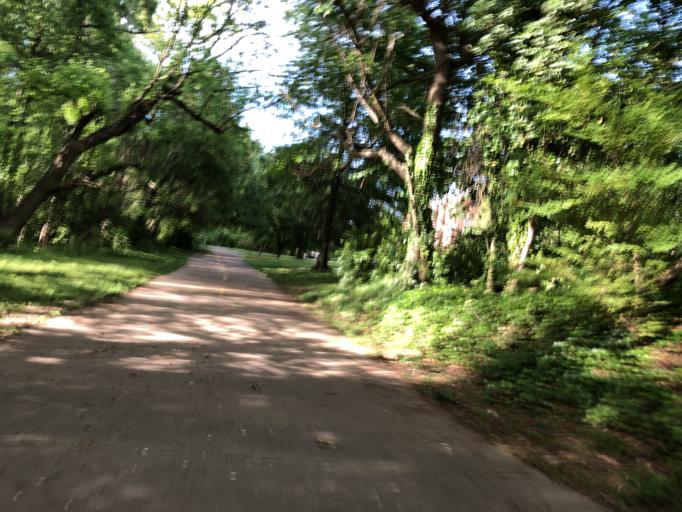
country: US
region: Georgia
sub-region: DeKalb County
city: Druid Hills
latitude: 33.7717
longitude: -84.3362
